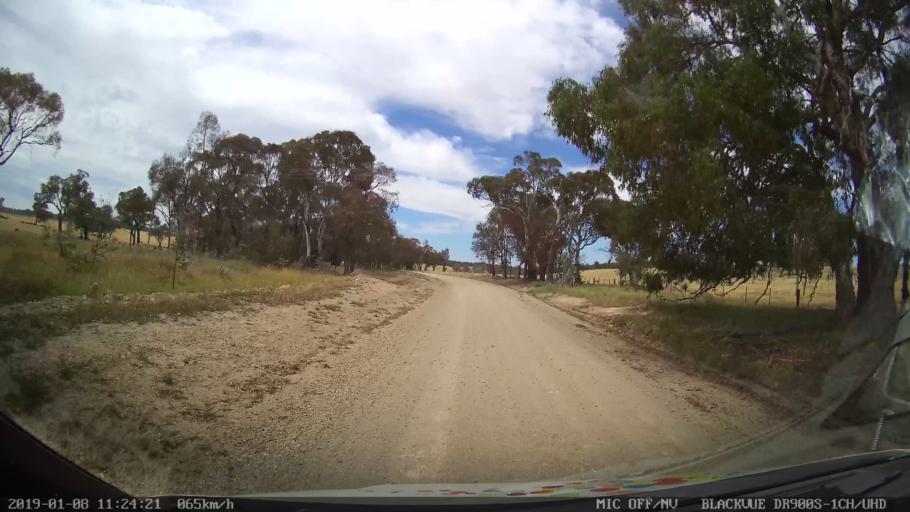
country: AU
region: New South Wales
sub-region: Guyra
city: Guyra
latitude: -30.2638
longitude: 151.5581
